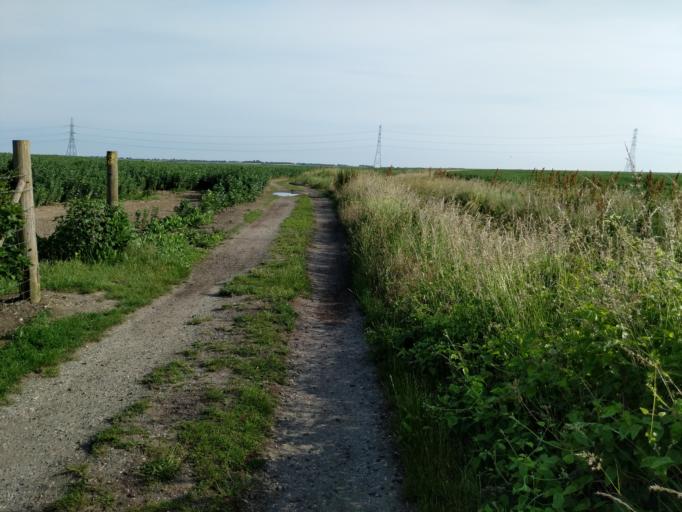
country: GB
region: England
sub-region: Kent
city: Faversham
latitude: 51.3324
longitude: 0.9146
